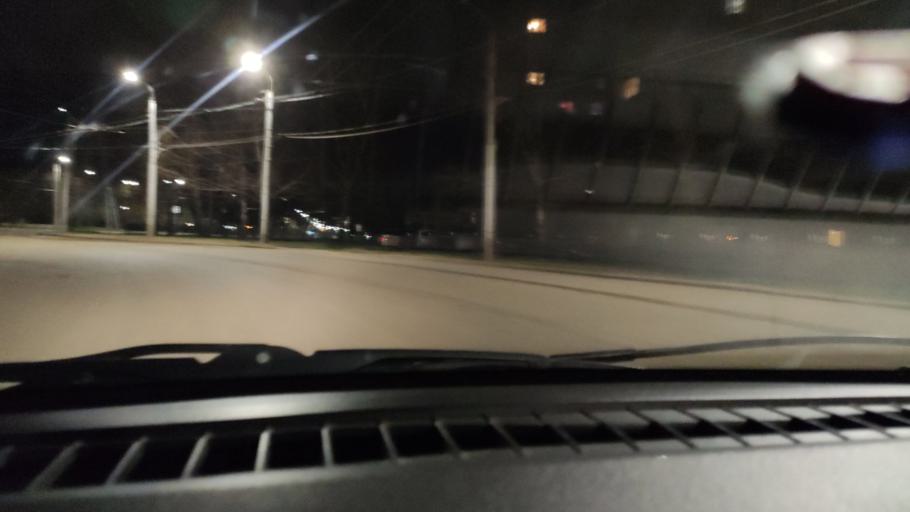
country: RU
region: Bashkortostan
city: Sterlitamak
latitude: 53.6377
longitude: 55.9109
